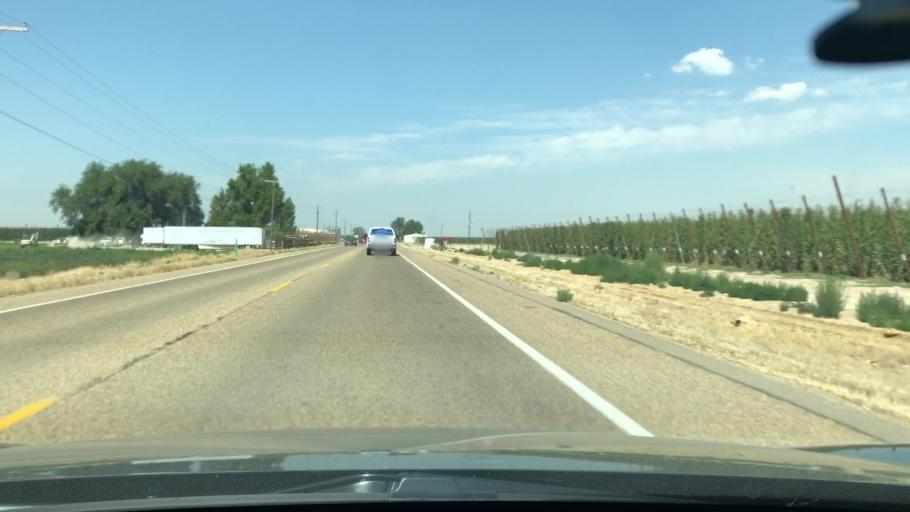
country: US
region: Idaho
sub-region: Canyon County
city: Wilder
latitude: 43.6885
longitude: -116.9120
